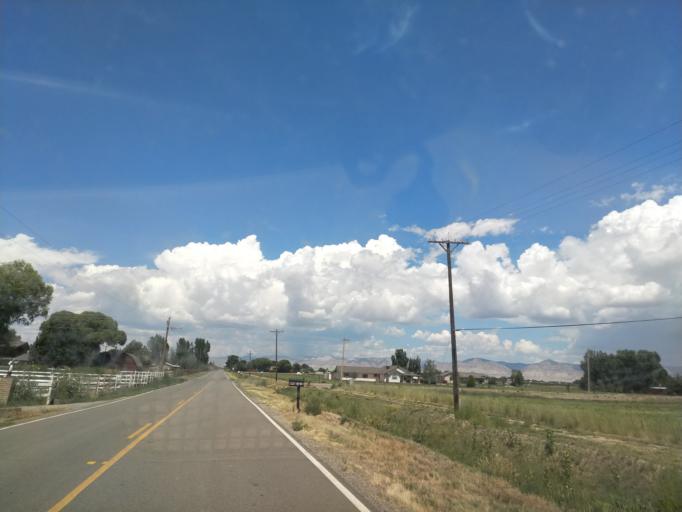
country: US
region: Colorado
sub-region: Mesa County
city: Redlands
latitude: 39.1343
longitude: -108.6639
